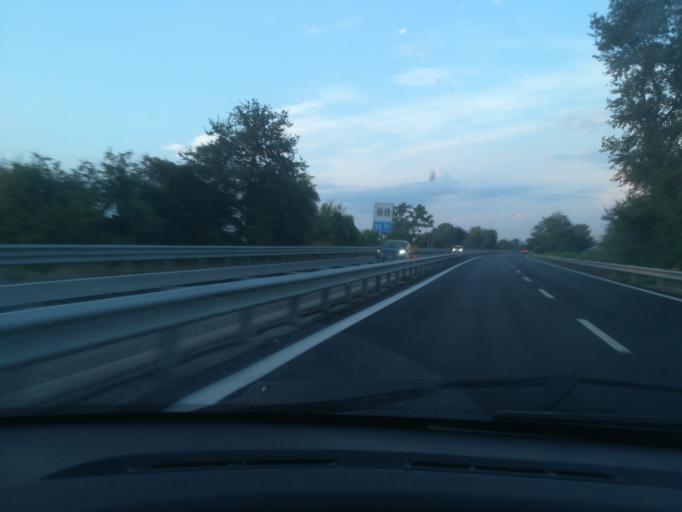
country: IT
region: The Marches
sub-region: Provincia di Macerata
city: Zona Industriale
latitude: 43.2611
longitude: 13.4717
